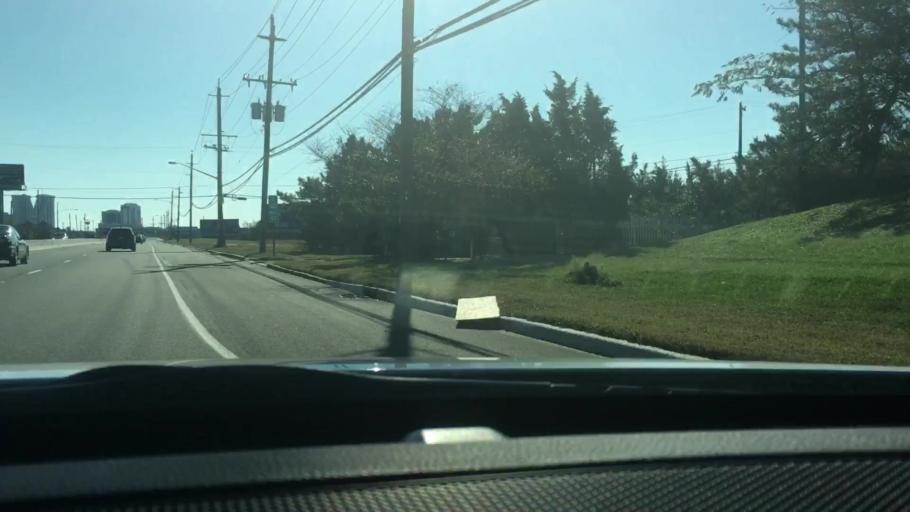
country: US
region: New Jersey
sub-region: Atlantic County
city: Ventnor City
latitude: 39.3647
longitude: -74.4695
